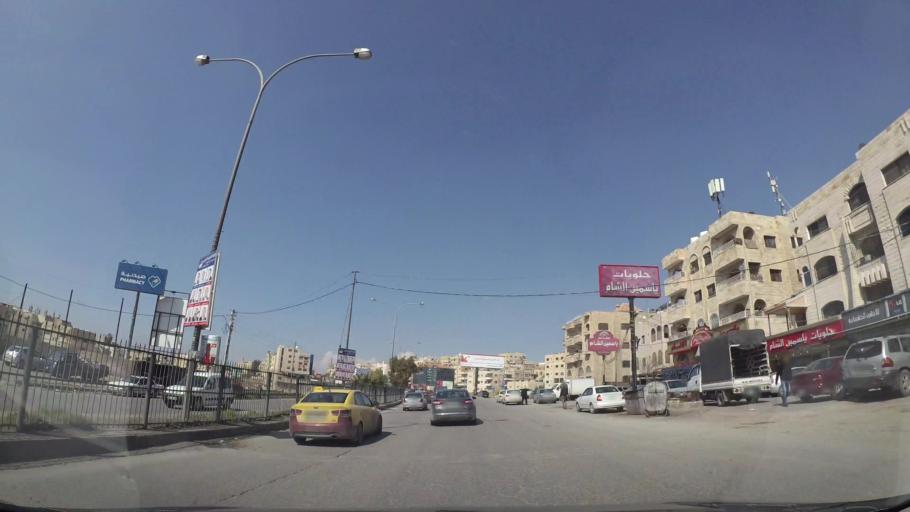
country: JO
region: Zarqa
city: Zarqa
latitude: 32.0422
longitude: 36.0942
